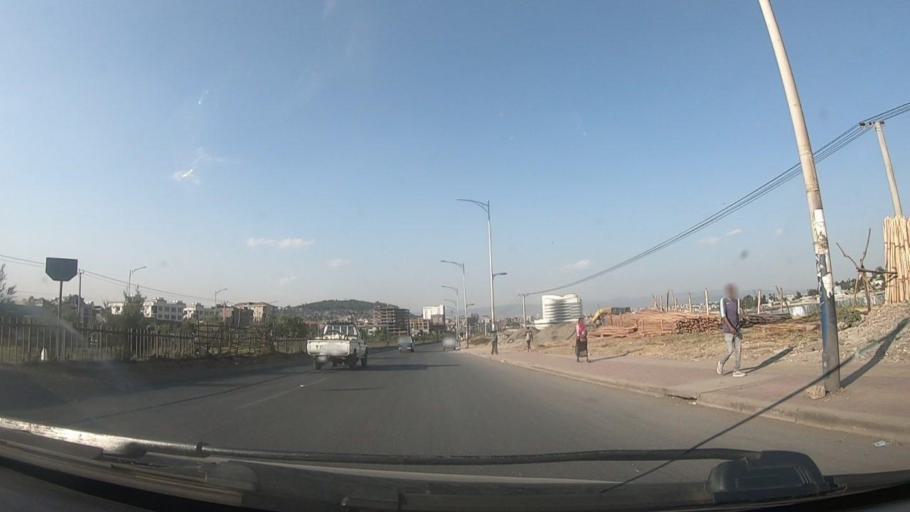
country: ET
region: Adis Abeba
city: Addis Ababa
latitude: 8.9284
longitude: 38.7342
